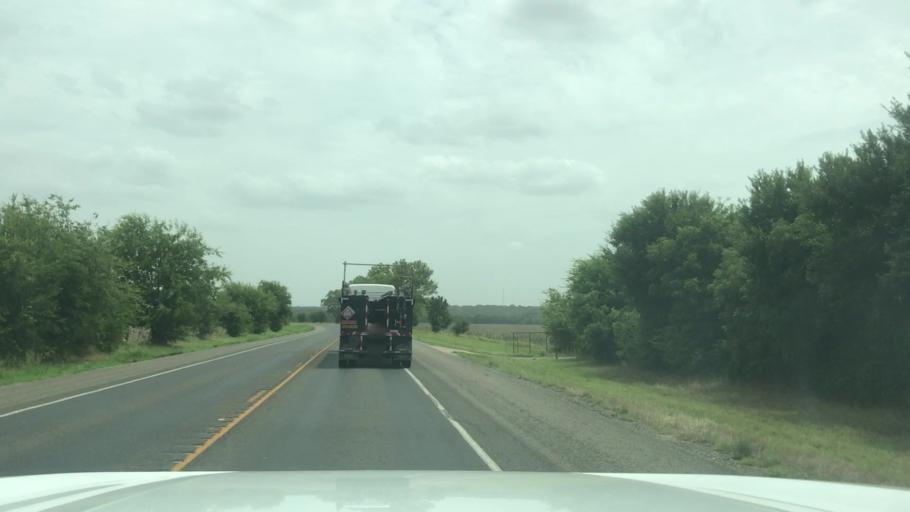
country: US
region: Texas
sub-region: Bosque County
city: Valley Mills
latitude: 31.6677
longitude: -97.4977
